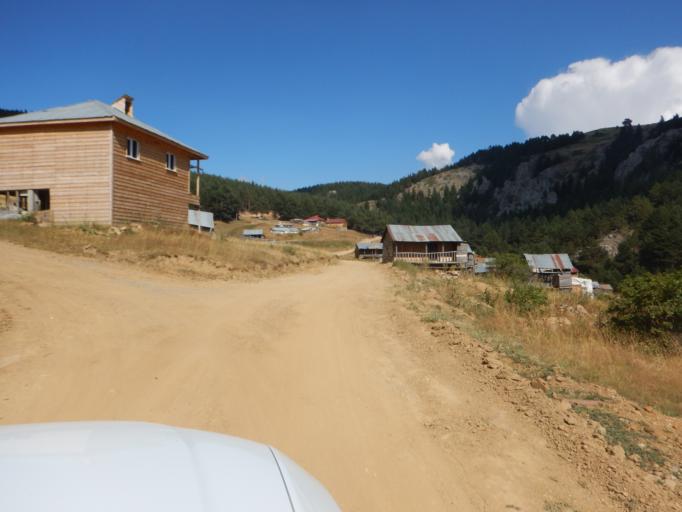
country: TR
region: Sivas
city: Ortakent
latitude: 40.5043
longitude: 38.0154
